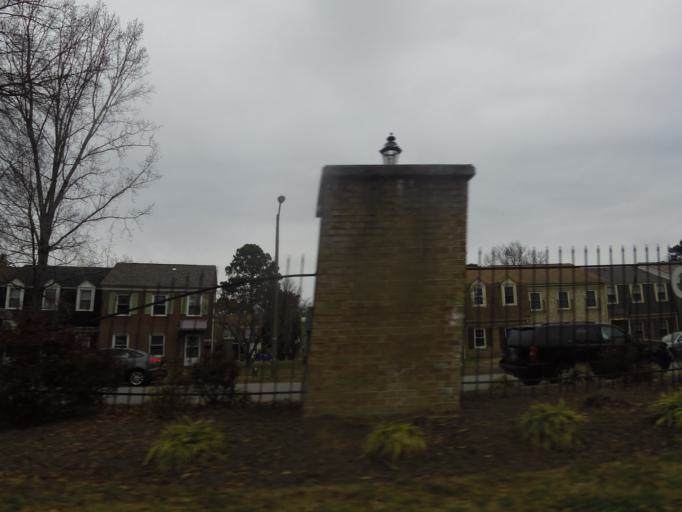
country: US
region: Virginia
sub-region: City of Portsmouth
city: Portsmouth Heights
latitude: 36.8552
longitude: -76.3835
